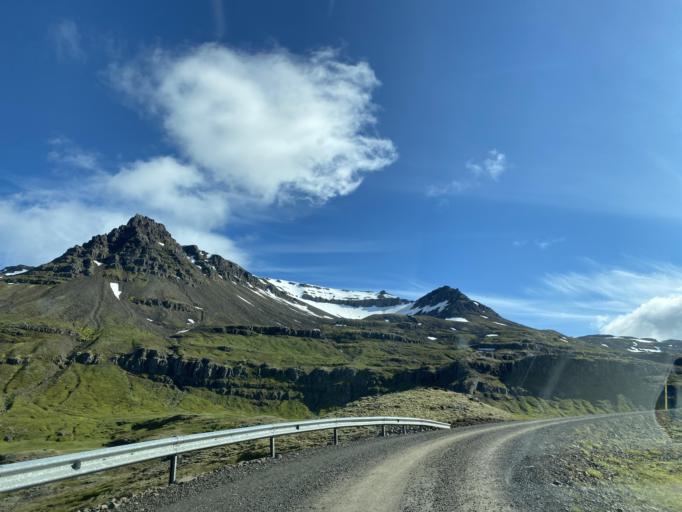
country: IS
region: East
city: Eskifjoerdur
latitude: 65.1796
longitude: -14.0874
